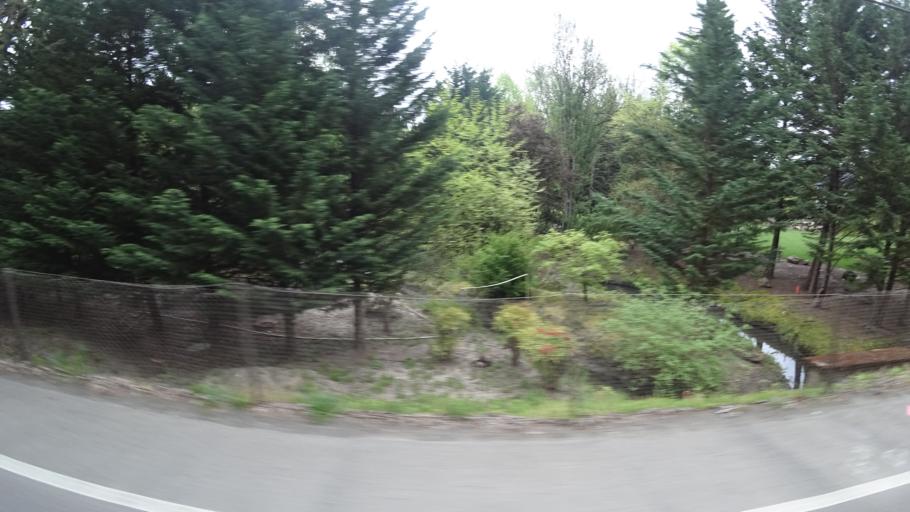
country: US
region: Oregon
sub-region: Washington County
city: Hillsboro
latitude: 45.5465
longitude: -122.9797
